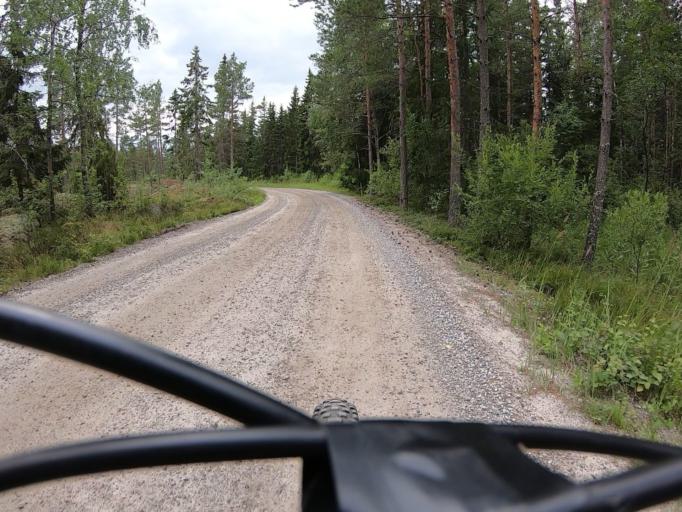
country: FI
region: Varsinais-Suomi
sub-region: Vakka-Suomi
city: Uusikaupunki
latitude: 60.8443
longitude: 21.3889
